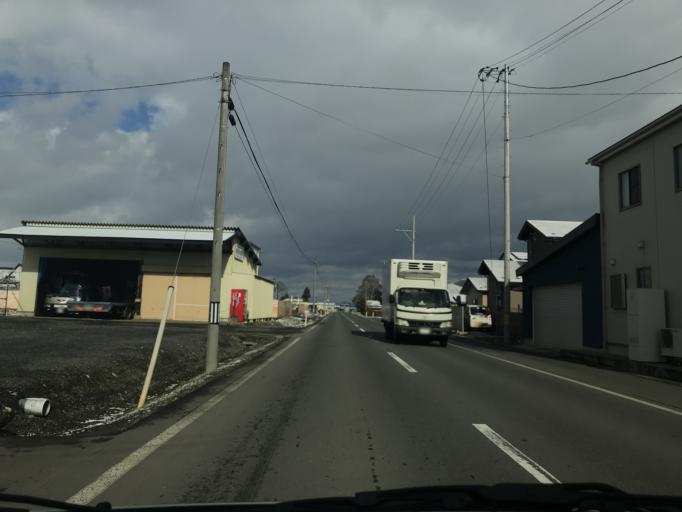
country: JP
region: Iwate
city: Mizusawa
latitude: 39.1455
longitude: 141.1138
